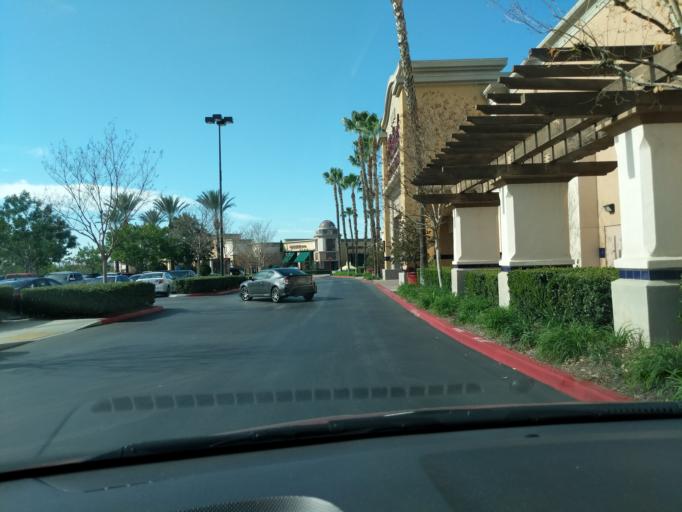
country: US
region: California
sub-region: San Bernardino County
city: Redlands
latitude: 34.0728
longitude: -117.2037
